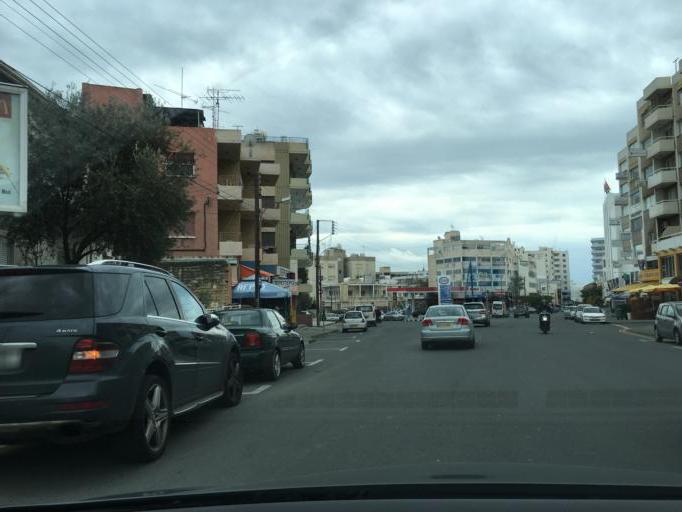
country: CY
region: Limassol
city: Limassol
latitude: 34.6840
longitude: 33.0442
